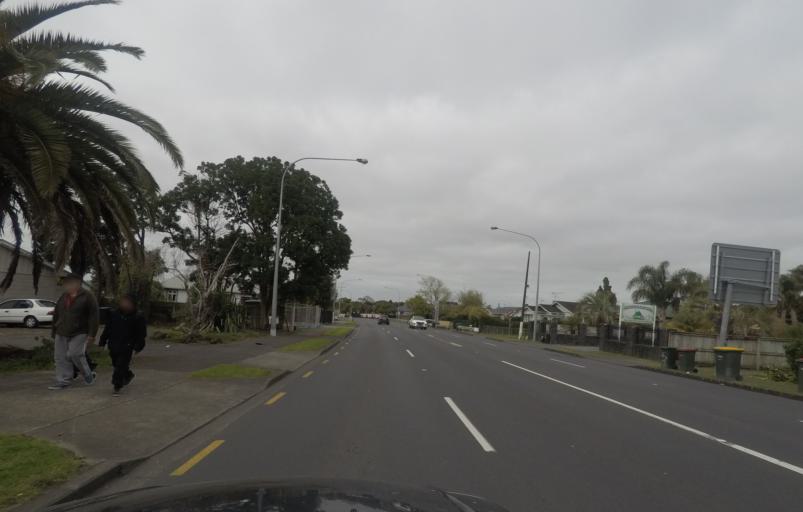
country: NZ
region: Auckland
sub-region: Auckland
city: Wiri
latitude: -36.9515
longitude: 174.8453
